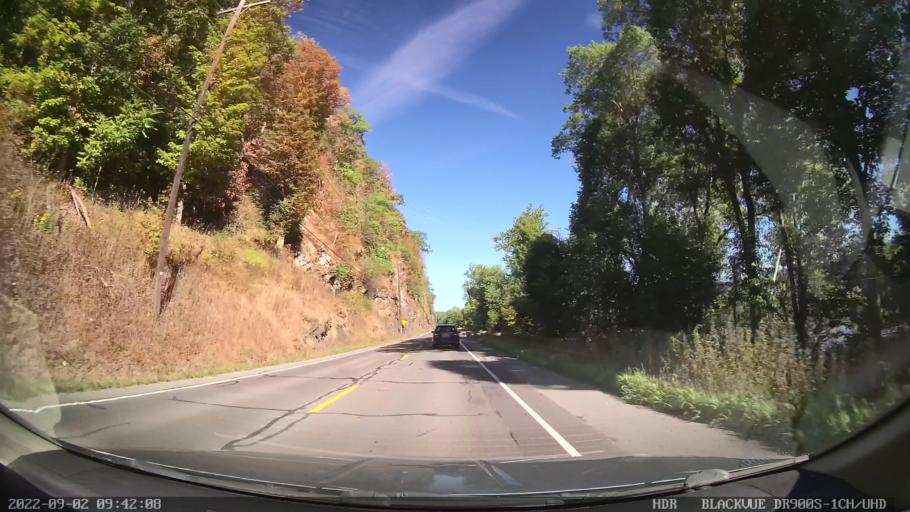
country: US
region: Pennsylvania
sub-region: Montour County
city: Danville
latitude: 40.9428
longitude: -76.6065
